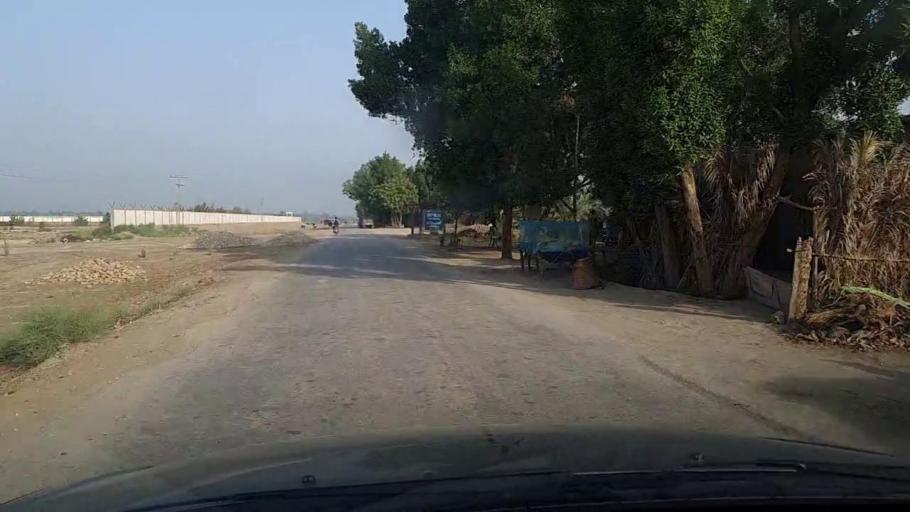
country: PK
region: Sindh
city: Khairpur
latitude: 27.5482
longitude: 68.6960
